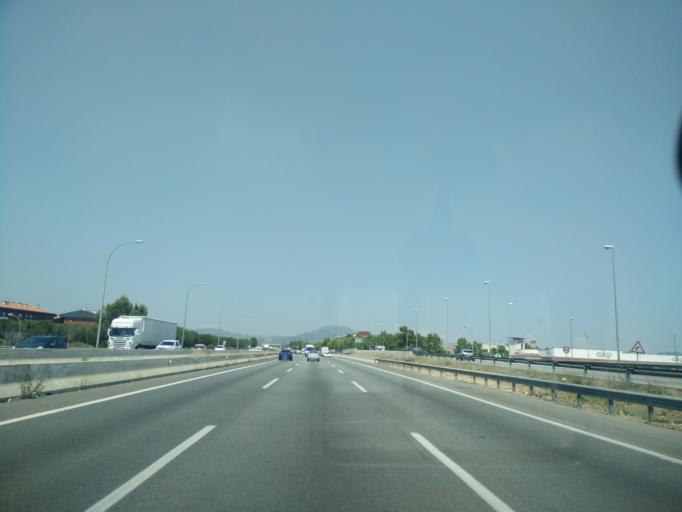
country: ES
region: Catalonia
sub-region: Provincia de Barcelona
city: Sant Quirze del Valles
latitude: 41.5311
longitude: 2.0925
